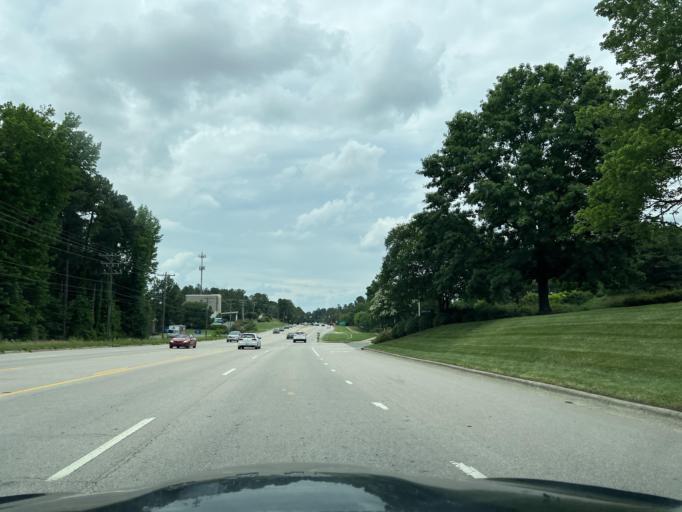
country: US
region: North Carolina
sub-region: Wake County
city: Morrisville
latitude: 35.8860
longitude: -78.8498
